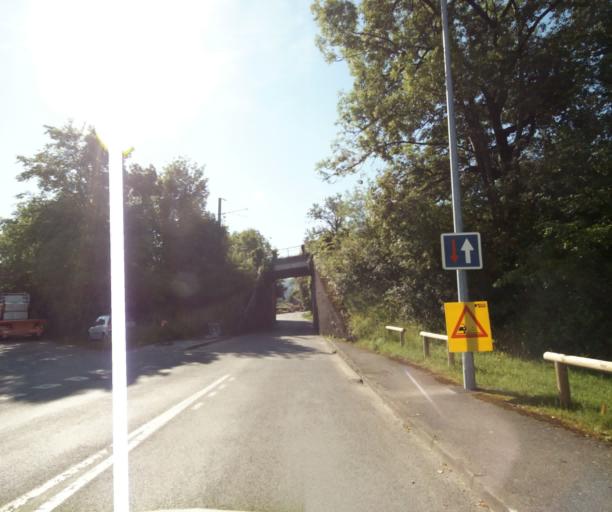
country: FR
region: Rhone-Alpes
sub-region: Departement de la Haute-Savoie
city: Thonon-les-Bains
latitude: 46.3850
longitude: 6.4981
